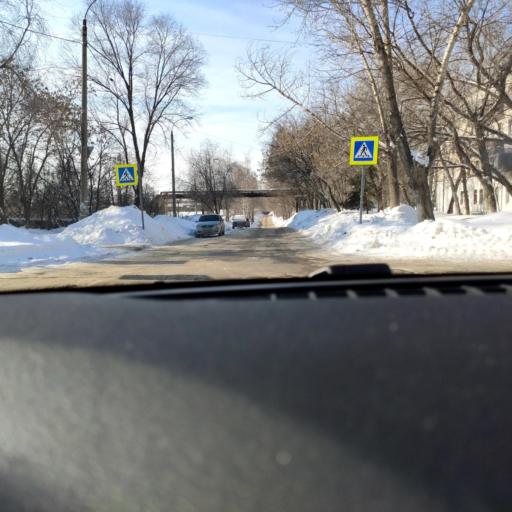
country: RU
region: Samara
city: Volzhskiy
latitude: 53.3427
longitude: 50.2205
